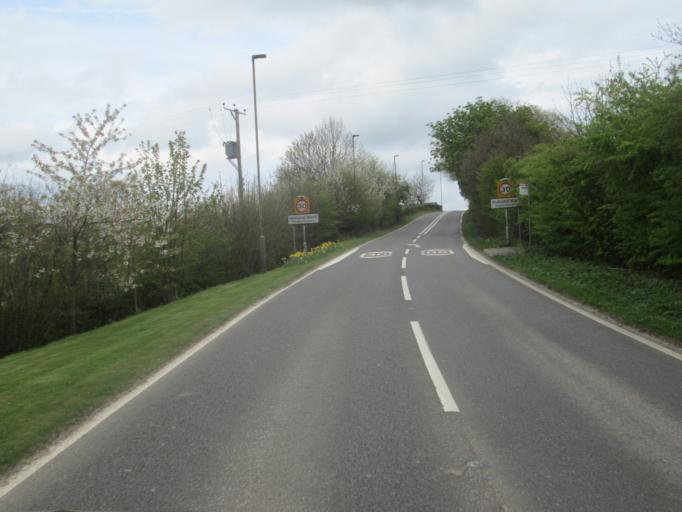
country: GB
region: England
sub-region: Derbyshire
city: Bradley
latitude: 53.0220
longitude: -1.6312
